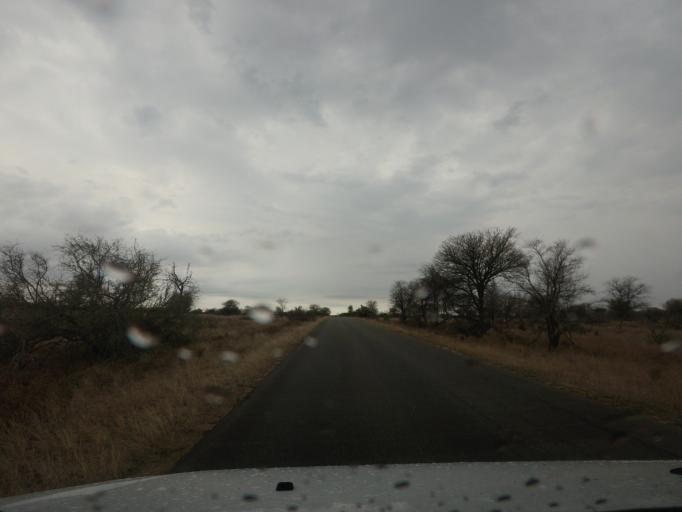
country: ZA
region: Limpopo
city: Thulamahashi
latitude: -24.4728
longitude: 31.4195
